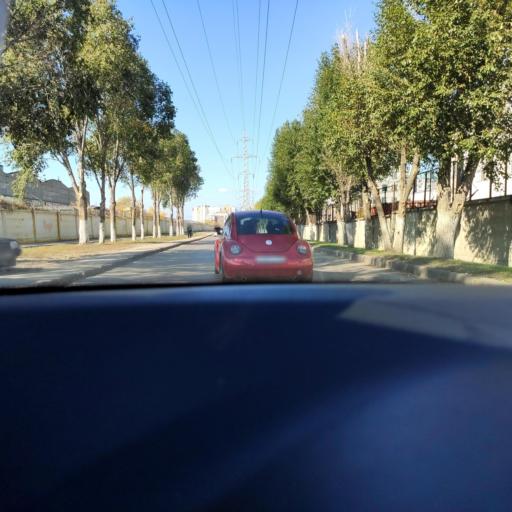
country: RU
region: Samara
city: Samara
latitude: 53.2410
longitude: 50.2051
